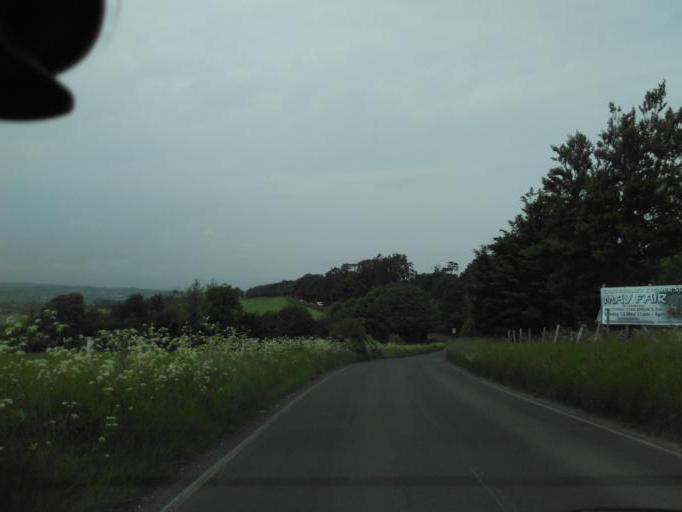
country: GB
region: England
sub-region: Kent
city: Chartham
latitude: 51.2436
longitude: 1.0330
